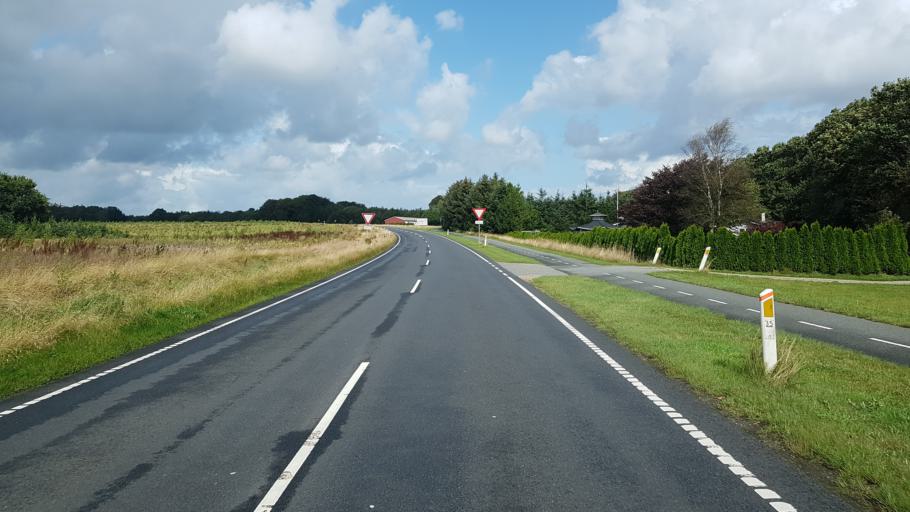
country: DK
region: South Denmark
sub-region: Vejen Kommune
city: Vejen
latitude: 55.5501
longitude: 9.1136
